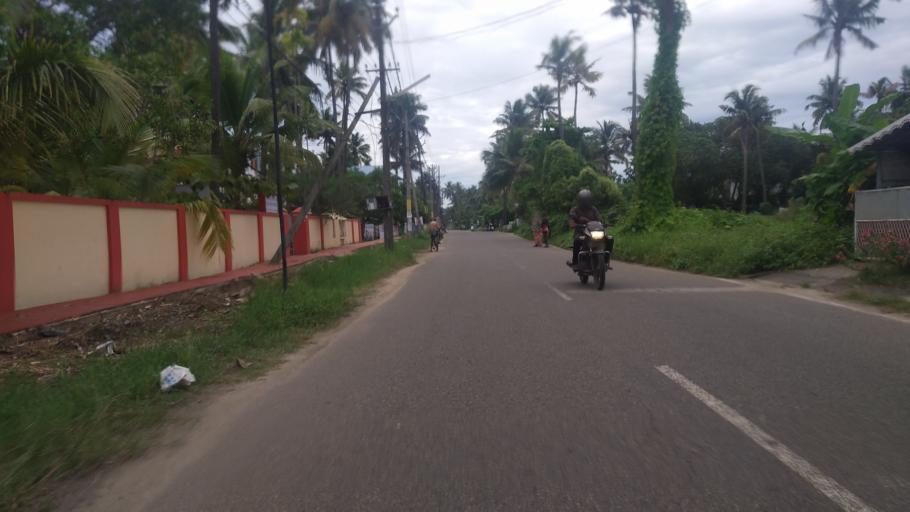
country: IN
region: Kerala
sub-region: Ernakulam
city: Cochin
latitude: 9.8884
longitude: 76.2605
